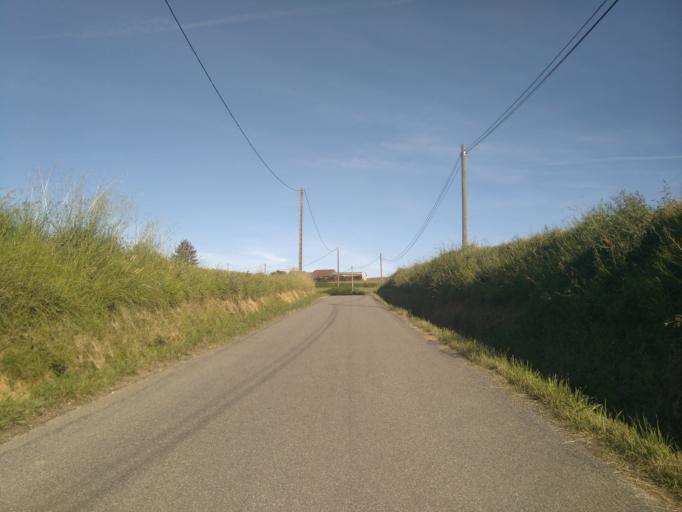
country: FR
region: Aquitaine
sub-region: Departement des Pyrenees-Atlantiques
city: Orthez
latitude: 43.4662
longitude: -0.7949
